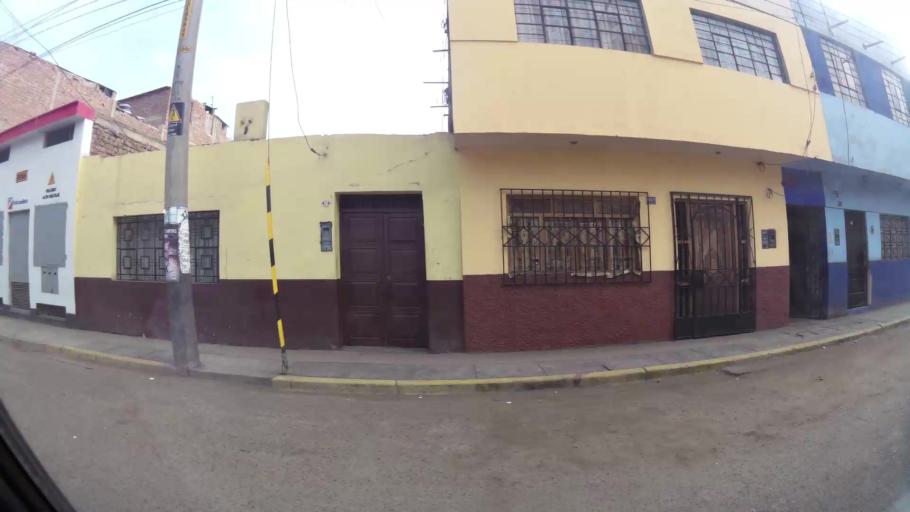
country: PE
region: La Libertad
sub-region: Provincia de Trujillo
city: Trujillo
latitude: -8.1156
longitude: -79.0216
